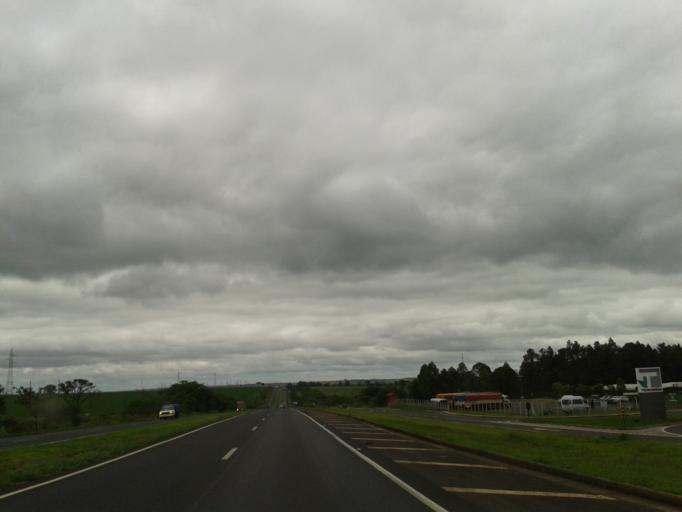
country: BR
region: Minas Gerais
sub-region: Uberlandia
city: Uberlandia
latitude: -19.0378
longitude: -48.2001
